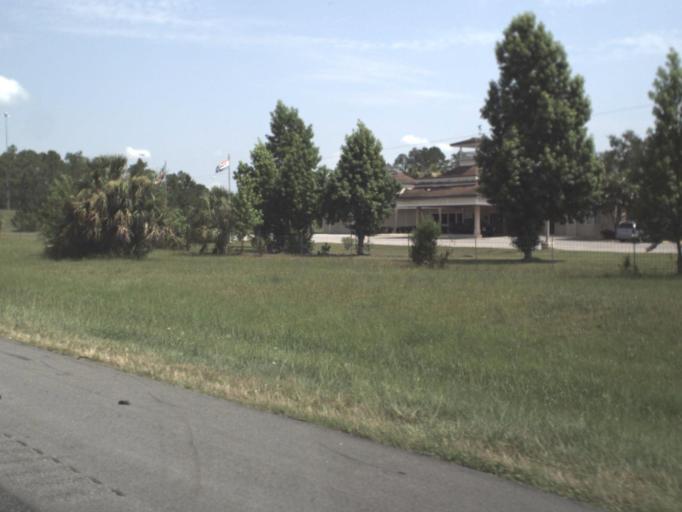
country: US
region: Georgia
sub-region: Echols County
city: Statenville
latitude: 30.5928
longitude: -83.1180
